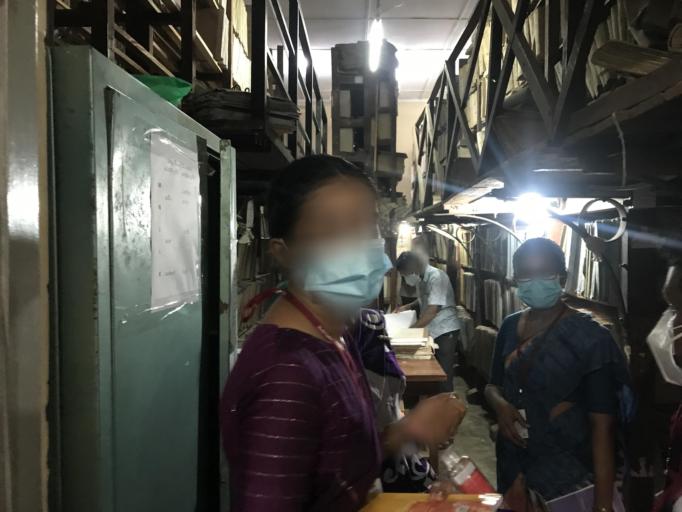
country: LK
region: Western
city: Gampaha
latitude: 7.0894
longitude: 79.9946
